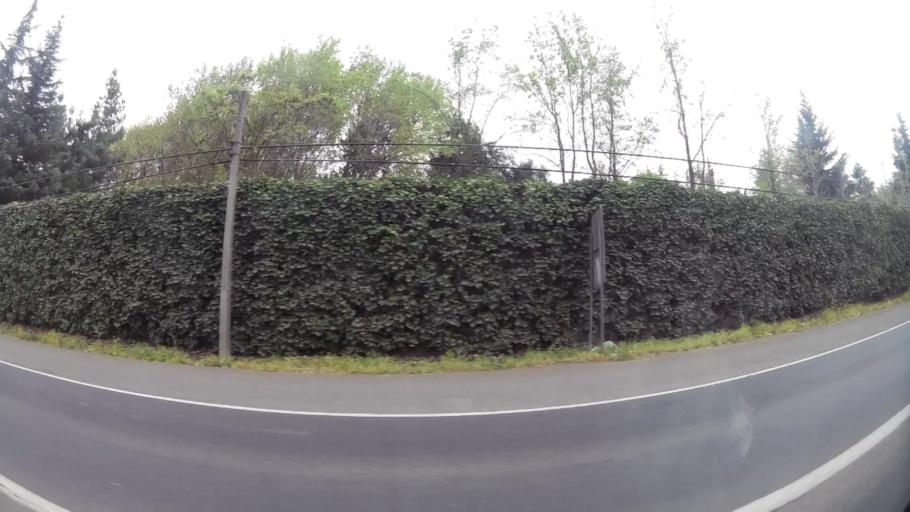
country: CL
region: Santiago Metropolitan
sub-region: Provincia de Chacabuco
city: Chicureo Abajo
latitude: -33.2435
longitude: -70.7055
